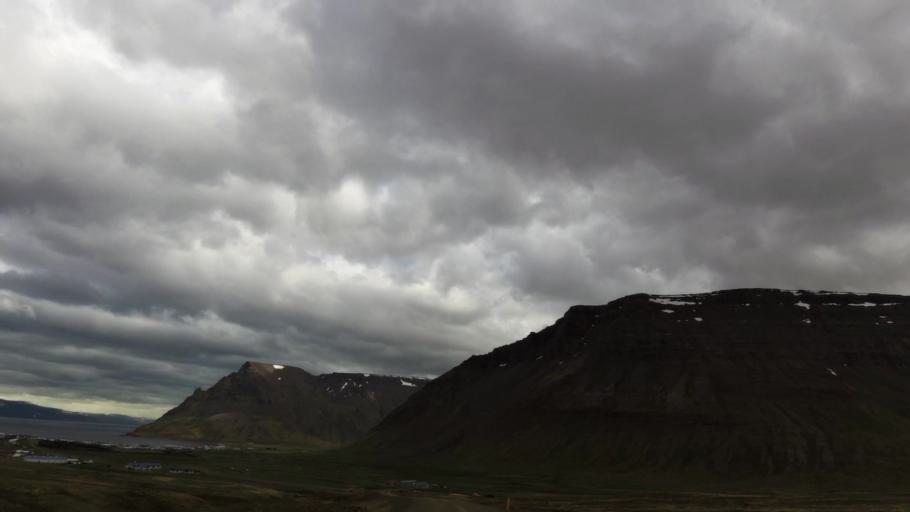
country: IS
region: Westfjords
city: Isafjoerdur
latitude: 66.1600
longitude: -23.2996
